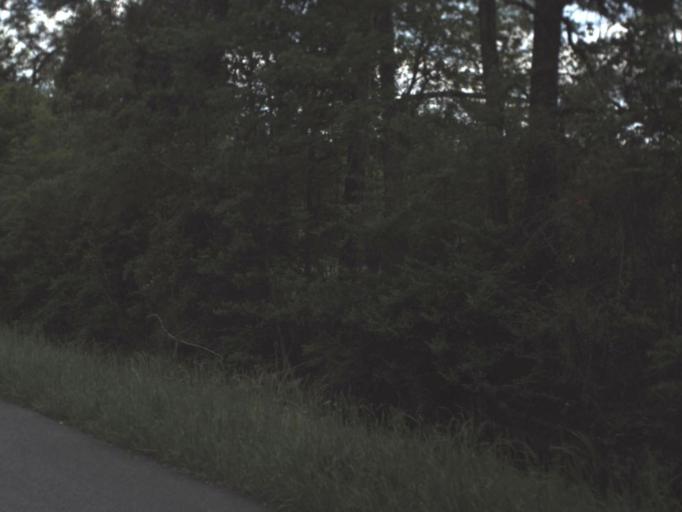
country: US
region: Florida
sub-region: Escambia County
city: Molino
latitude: 30.7948
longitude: -87.4195
